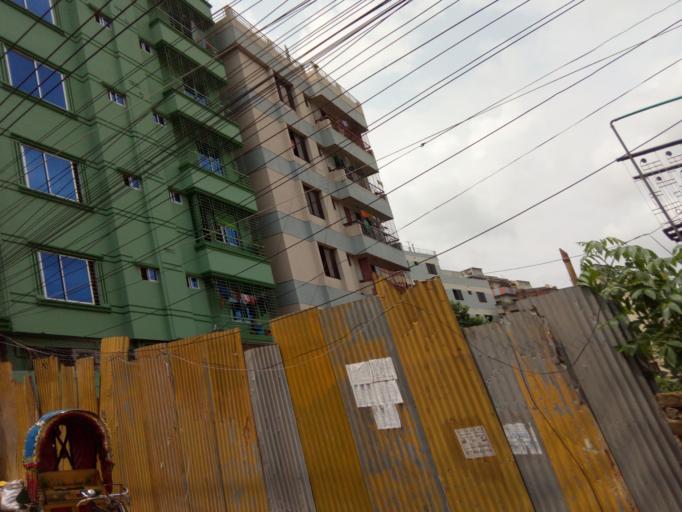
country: BD
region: Dhaka
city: Azimpur
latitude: 23.7469
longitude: 90.3648
